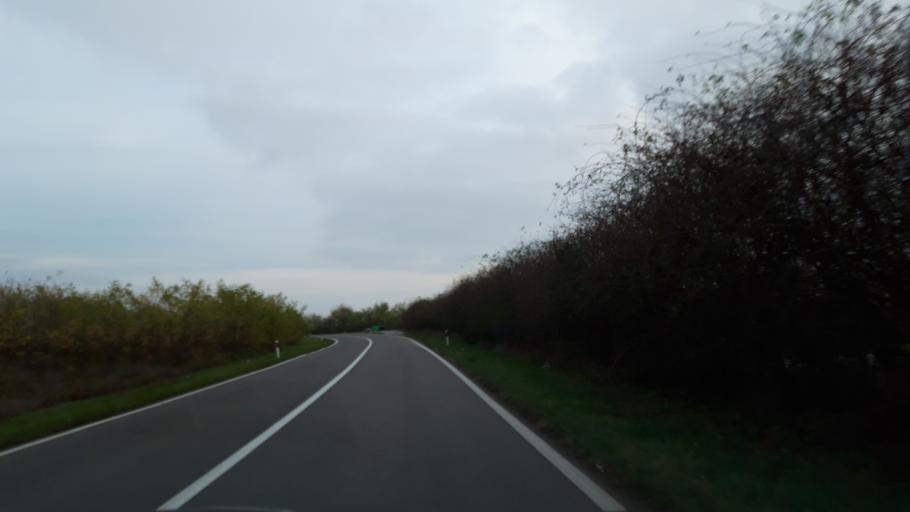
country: RS
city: Sanad
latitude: 45.9667
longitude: 20.1256
